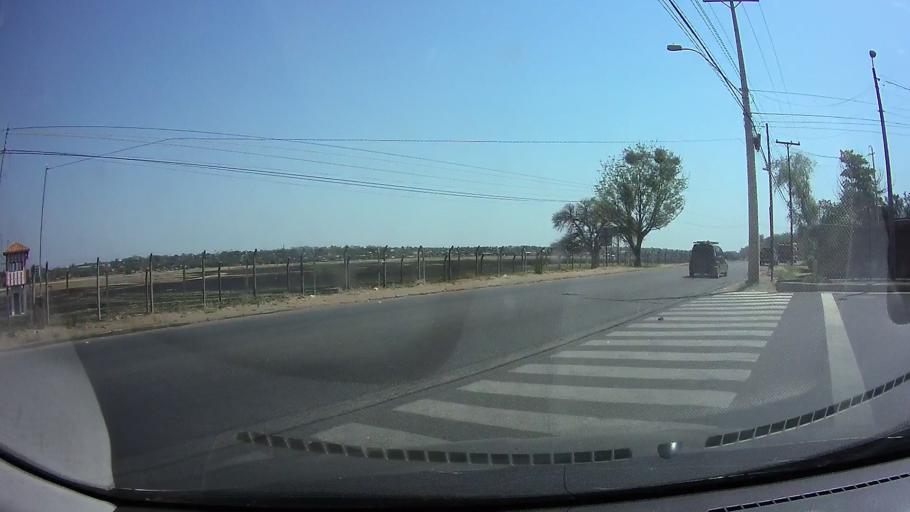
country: PY
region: Central
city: Limpio
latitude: -25.2270
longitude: -57.5105
